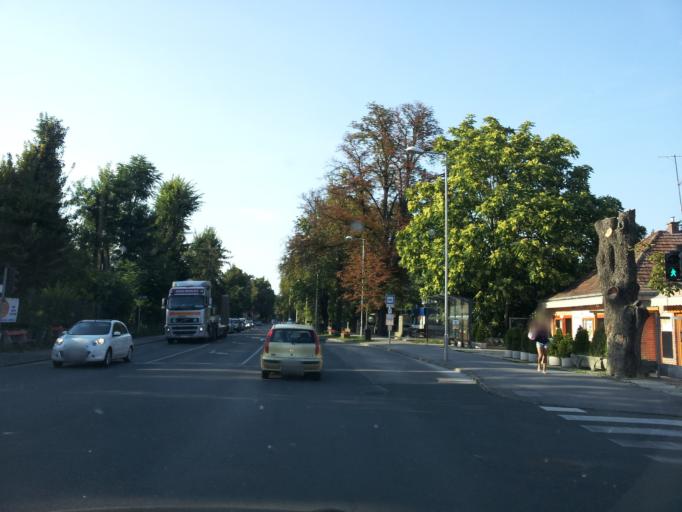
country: HU
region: Pest
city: Leanyfalu
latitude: 47.7188
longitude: 19.0894
